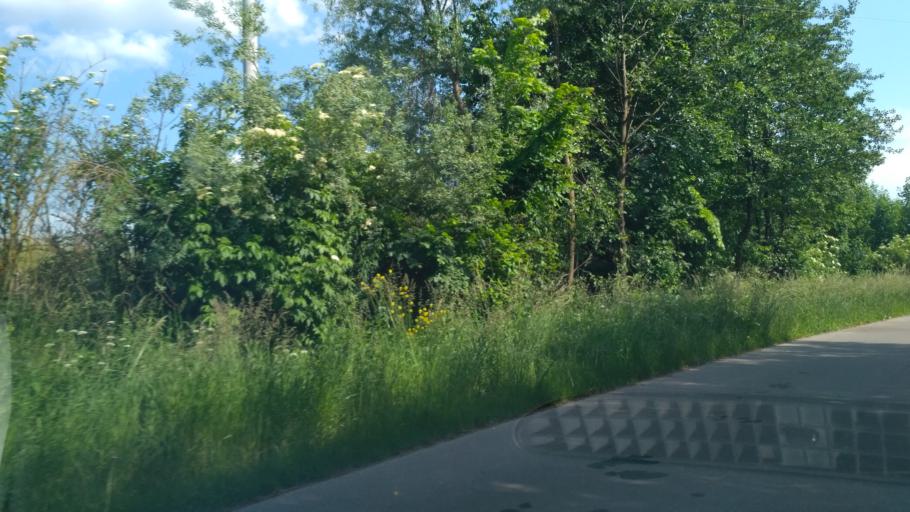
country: PL
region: Subcarpathian Voivodeship
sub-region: Powiat jaroslawski
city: Ostrow
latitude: 49.9384
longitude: 22.7399
